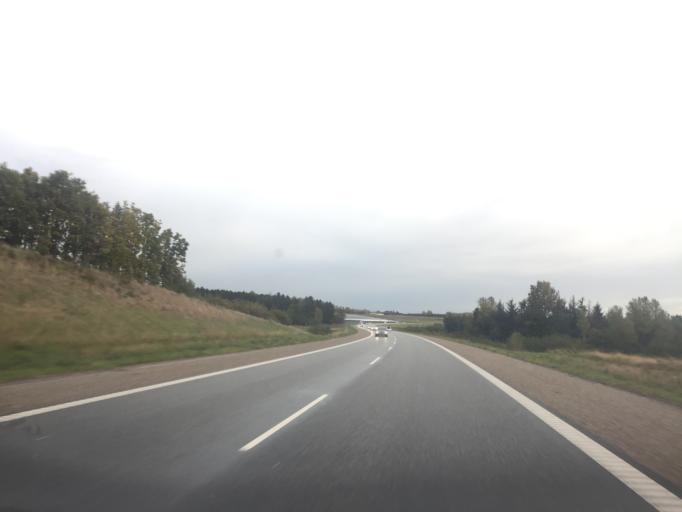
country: DK
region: Capital Region
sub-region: Egedal Kommune
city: Smorumnedre
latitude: 55.7271
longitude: 12.2844
